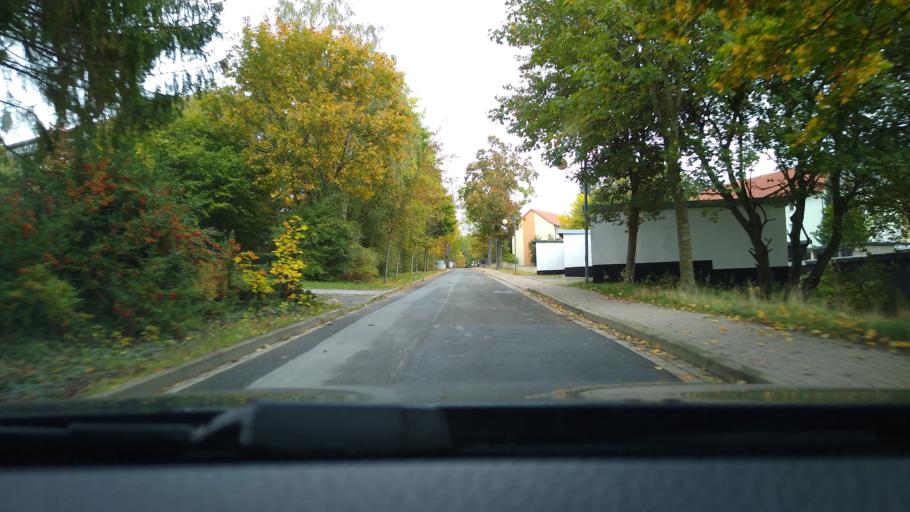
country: DE
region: Saxony-Anhalt
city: Elbingerode
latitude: 51.7709
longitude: 10.7900
